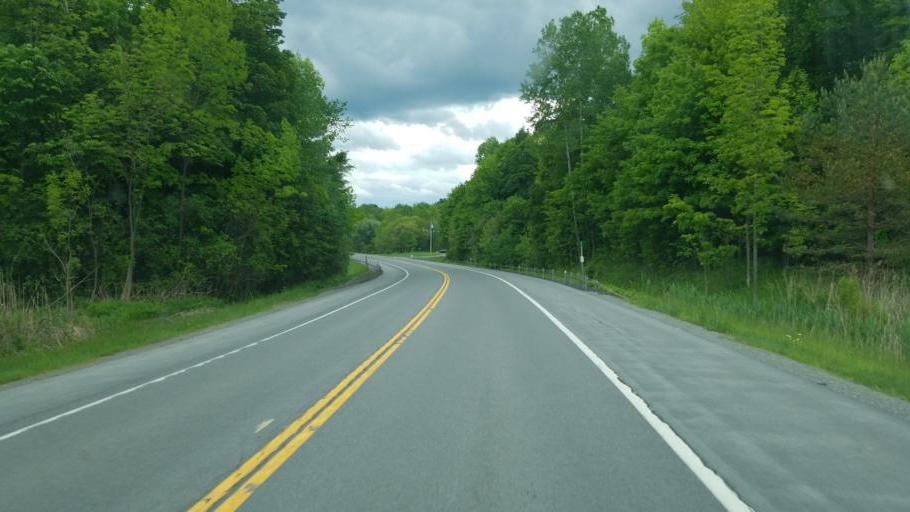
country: US
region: New York
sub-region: Oneida County
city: Chadwicks
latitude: 42.9682
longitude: -75.2518
